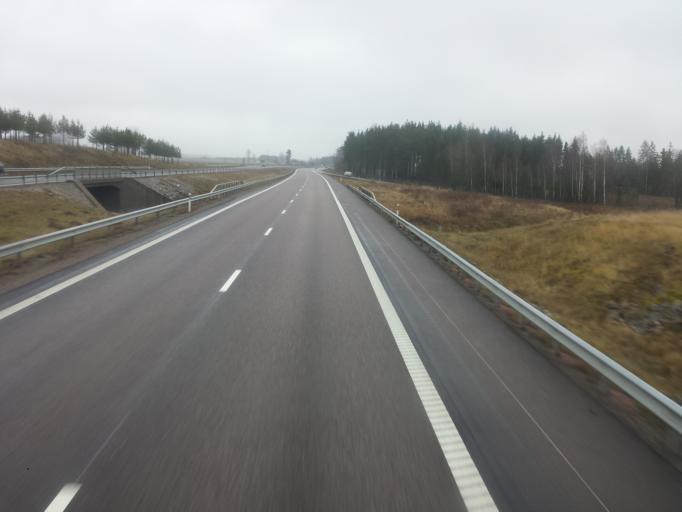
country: SE
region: Soedermanland
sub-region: Nykopings Kommun
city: Stigtomta
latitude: 58.7550
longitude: 16.7300
